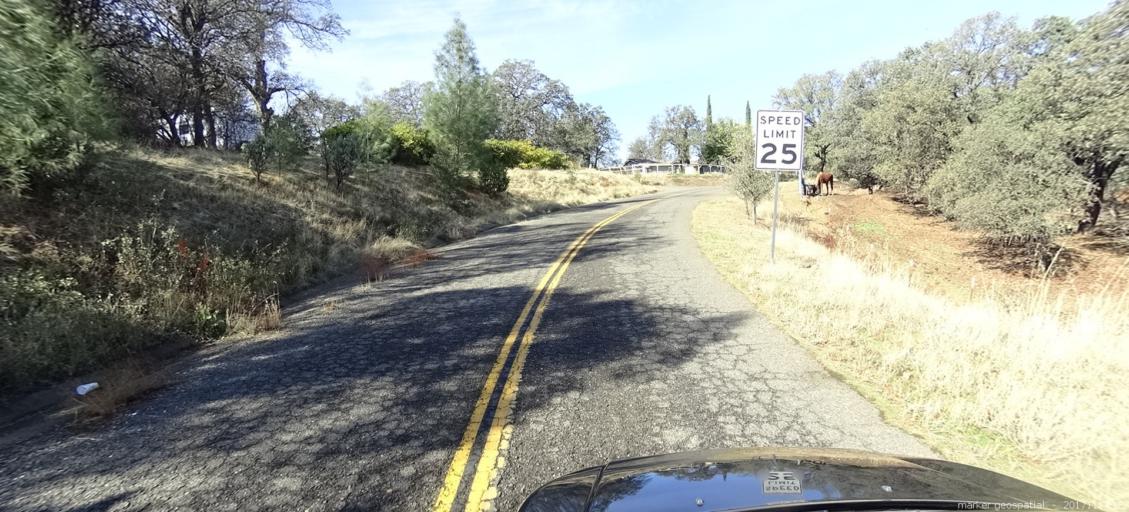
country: US
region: California
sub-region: Shasta County
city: Anderson
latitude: 40.4010
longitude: -122.4073
